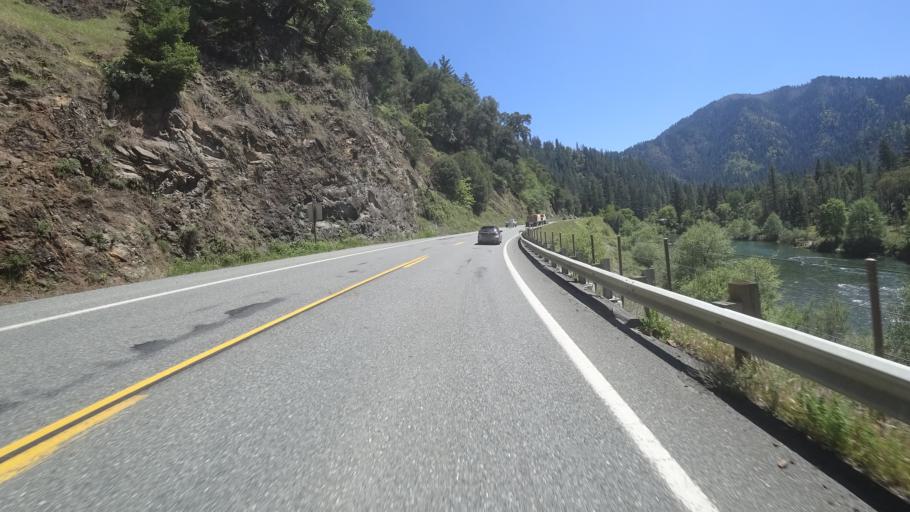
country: US
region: California
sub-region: Trinity County
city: Hayfork
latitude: 40.7842
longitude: -123.3360
